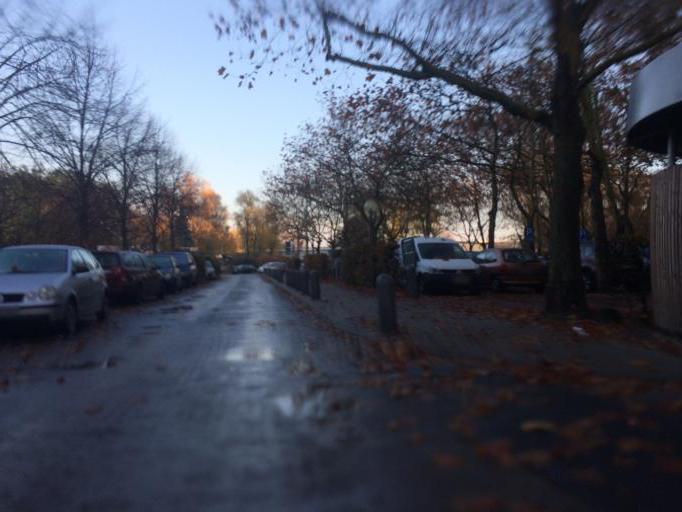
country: DE
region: Berlin
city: Markisches Viertel
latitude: 52.6069
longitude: 13.3624
